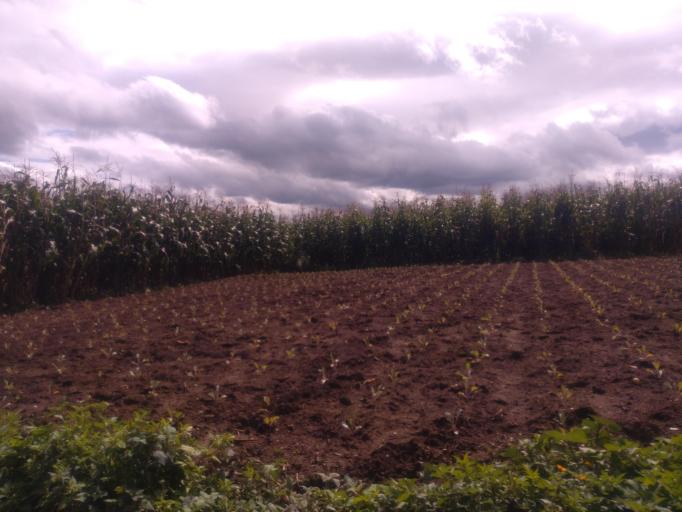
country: GT
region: Quetzaltenango
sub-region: Municipio de La Esperanza
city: La Esperanza
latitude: 14.8576
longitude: -91.5700
